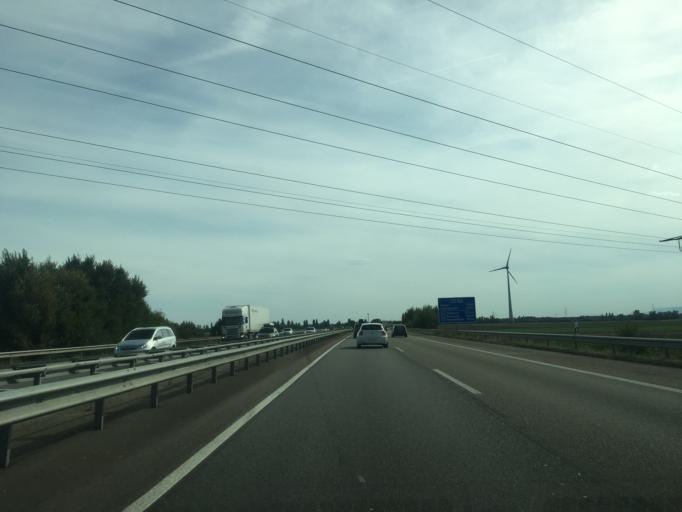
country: DE
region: Rheinland-Pfalz
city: Hessheim
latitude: 49.5387
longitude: 8.3159
